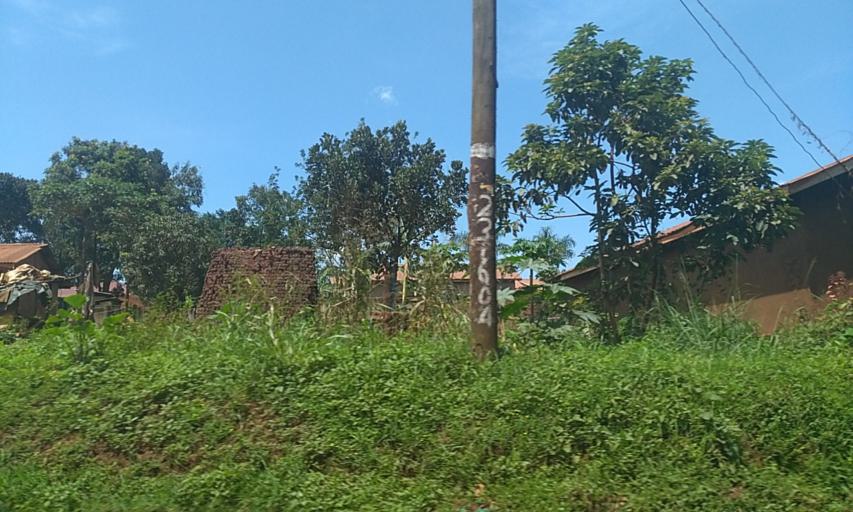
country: UG
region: Central Region
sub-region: Wakiso District
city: Wakiso
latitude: 0.4015
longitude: 32.4861
